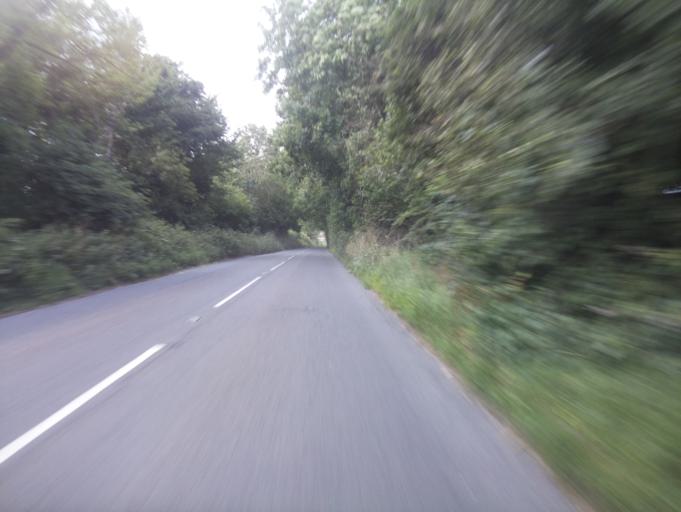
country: GB
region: England
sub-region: Gloucestershire
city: Chipping Campden
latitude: 52.0059
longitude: -1.7613
